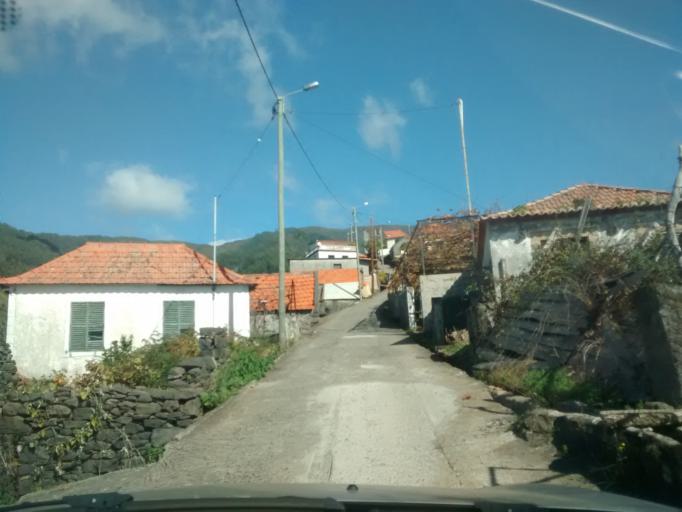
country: PT
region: Madeira
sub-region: Calheta
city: Arco da Calheta
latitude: 32.7304
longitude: -17.1610
